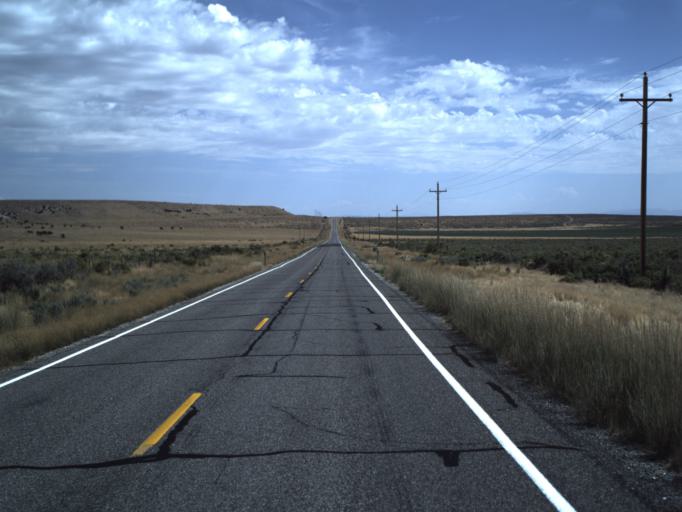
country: US
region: Idaho
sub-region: Cassia County
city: Burley
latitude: 41.8166
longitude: -113.2401
